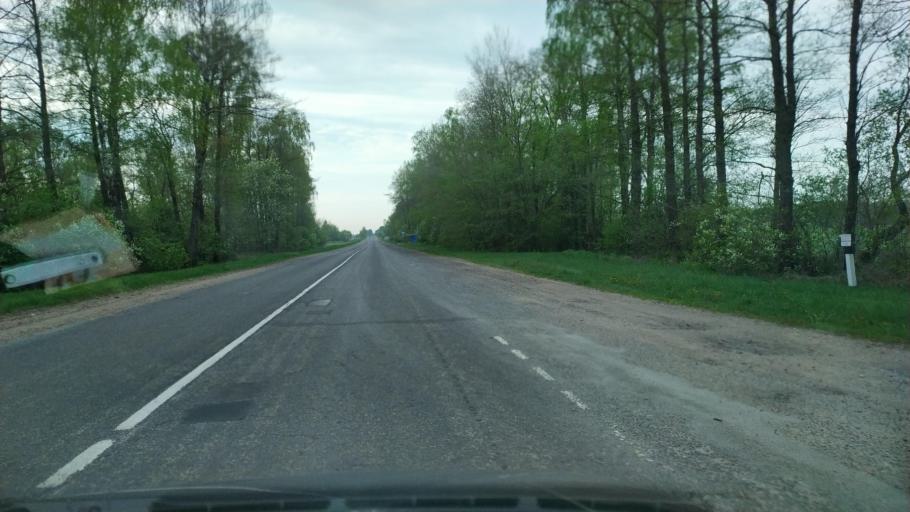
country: BY
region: Brest
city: Zhabinka
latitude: 52.2658
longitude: 23.9592
